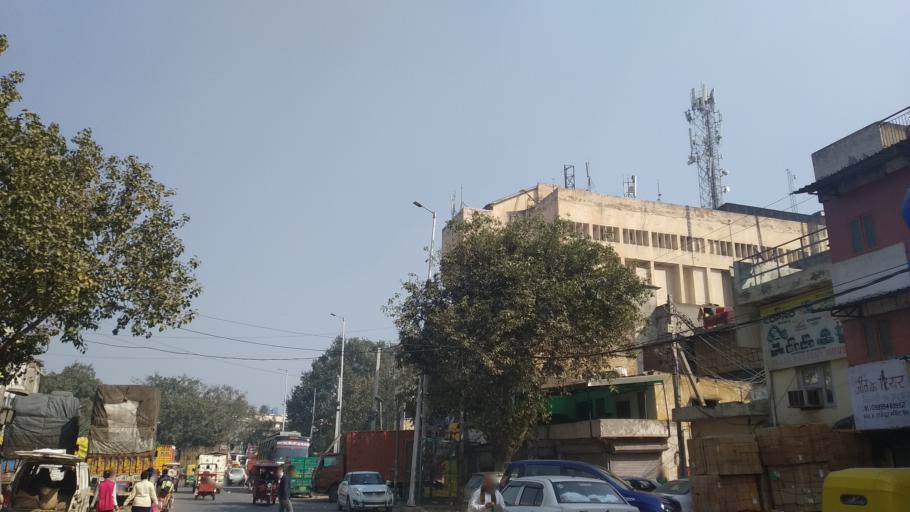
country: IN
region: NCT
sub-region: North Delhi
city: Delhi
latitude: 28.6641
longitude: 77.2181
